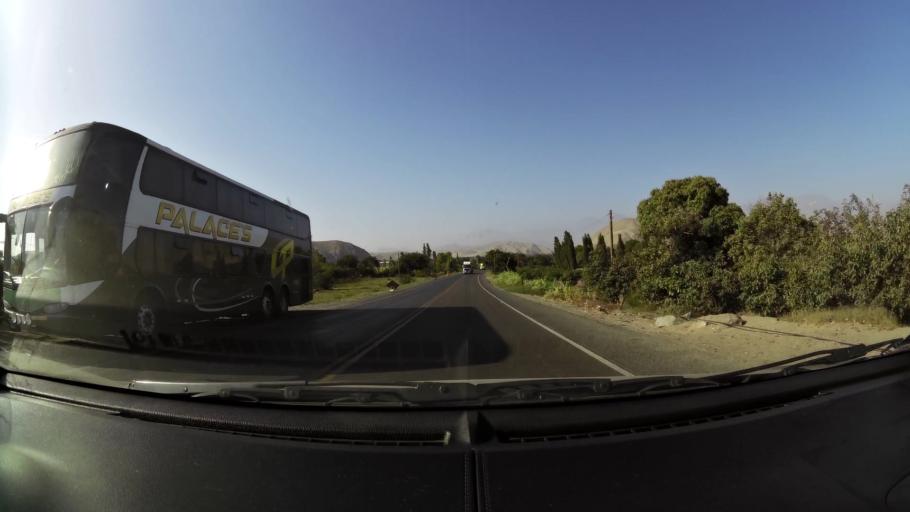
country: PE
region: Ancash
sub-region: Provincia de Casma
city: Casma
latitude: -9.4973
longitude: -78.2777
